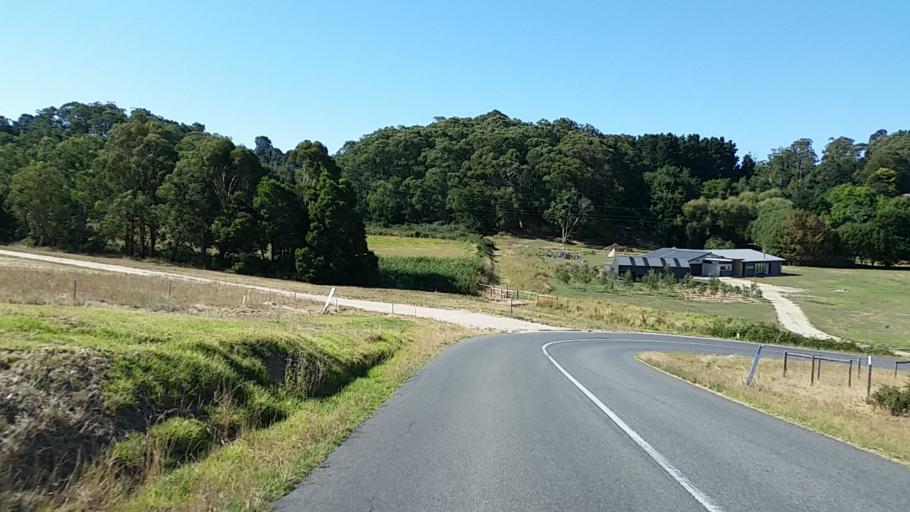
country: AU
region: South Australia
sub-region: Adelaide Hills
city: Bridgewater
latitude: -34.9671
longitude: 138.7332
